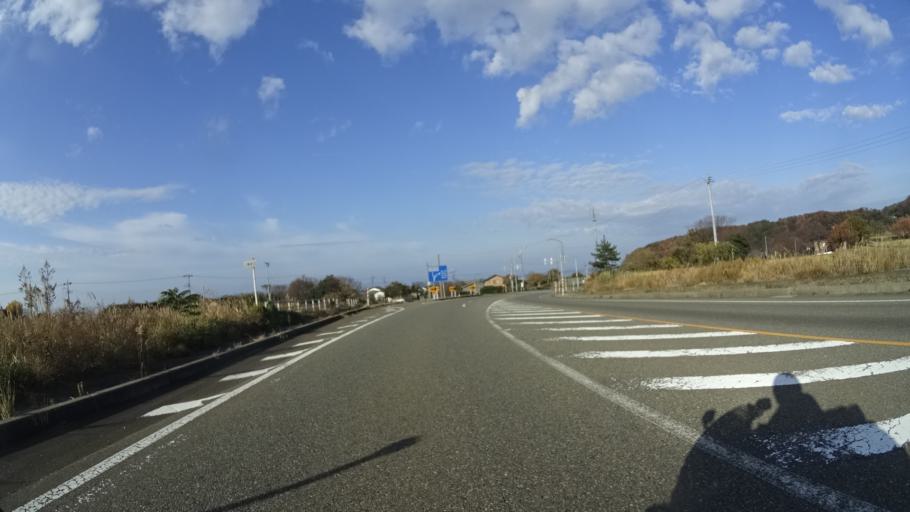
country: JP
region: Niigata
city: Kashiwazaki
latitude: 37.3280
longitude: 138.4557
